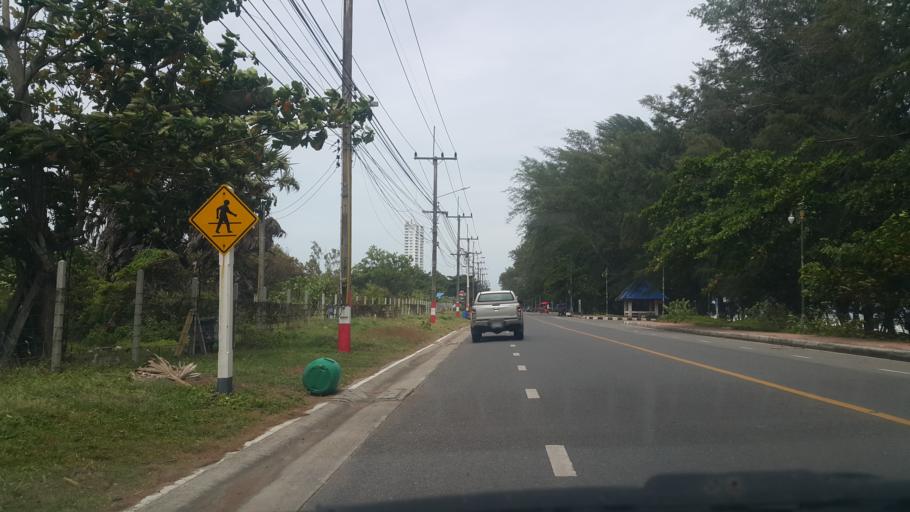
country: TH
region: Rayong
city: Rayong
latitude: 12.6164
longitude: 101.3758
